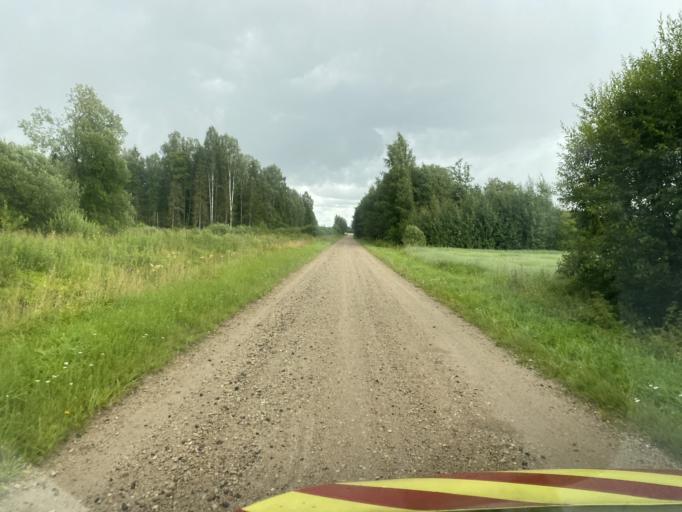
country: EE
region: Valgamaa
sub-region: Torva linn
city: Torva
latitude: 58.0933
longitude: 25.9255
